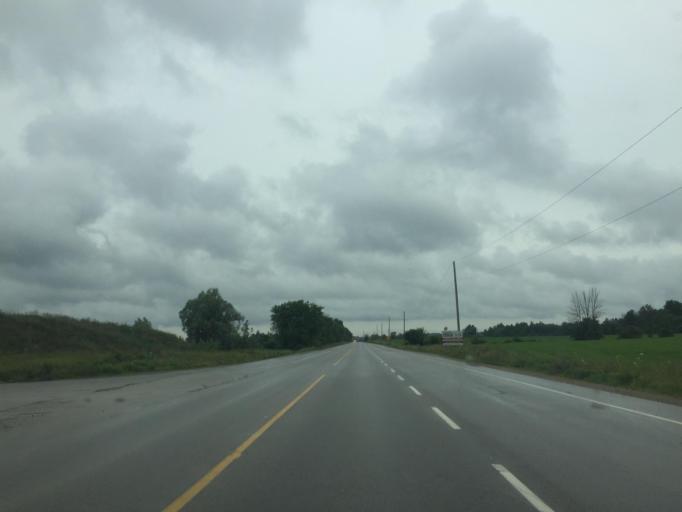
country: CA
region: Ontario
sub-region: Wellington County
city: Guelph
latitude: 43.4821
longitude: -80.2282
